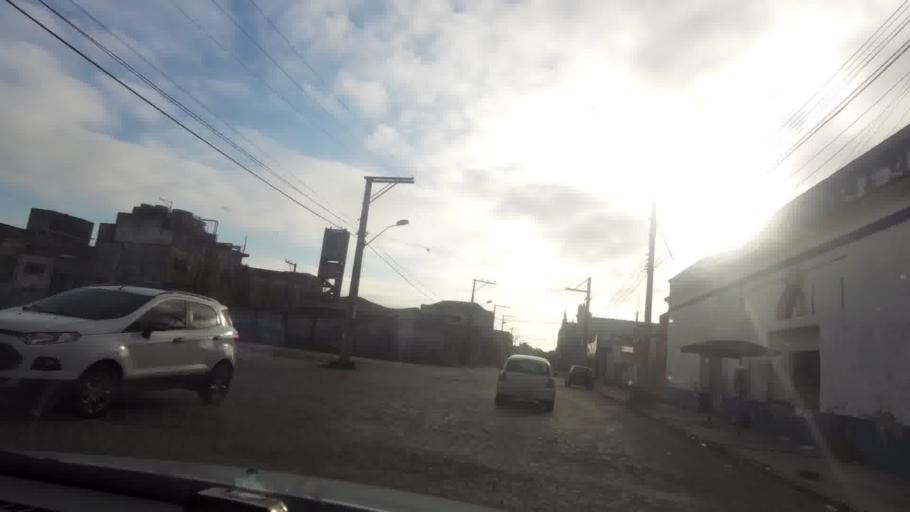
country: BR
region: Rio Grande do Sul
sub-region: Rio Grande
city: Rio Grande
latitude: -32.0317
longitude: -52.0880
